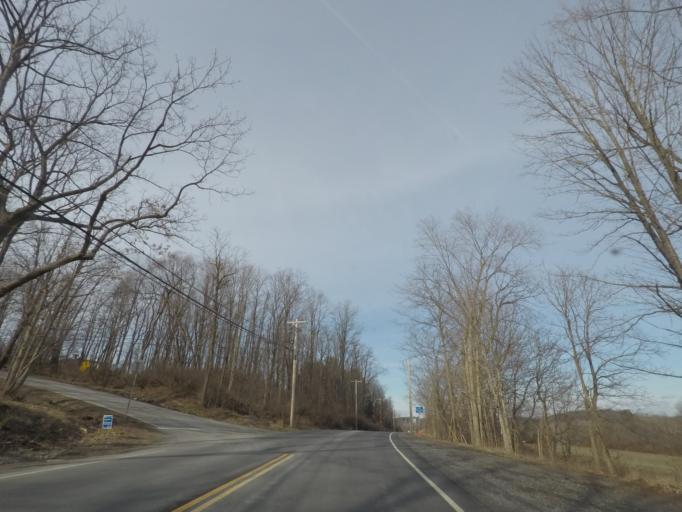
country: US
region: New York
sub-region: Columbia County
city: Valatie
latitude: 42.3870
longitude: -73.6433
